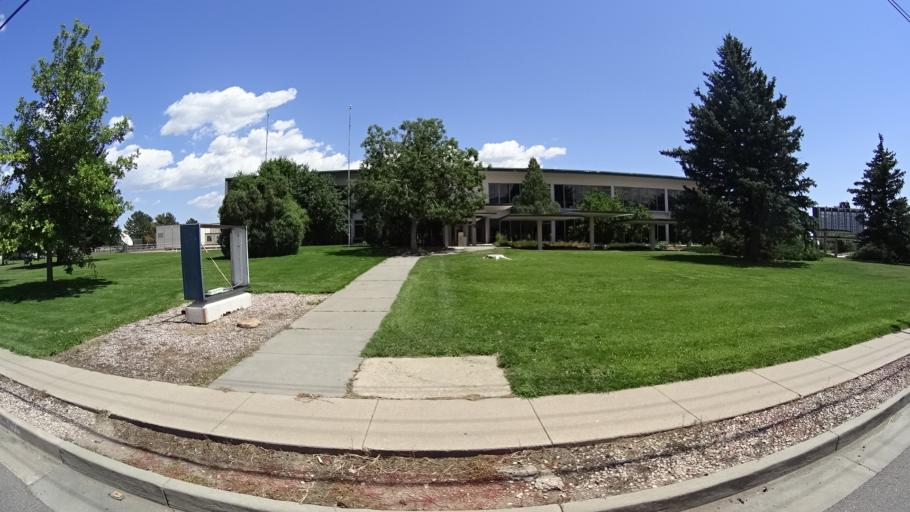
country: US
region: Colorado
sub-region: El Paso County
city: Colorado Springs
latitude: 38.8270
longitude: -104.7949
